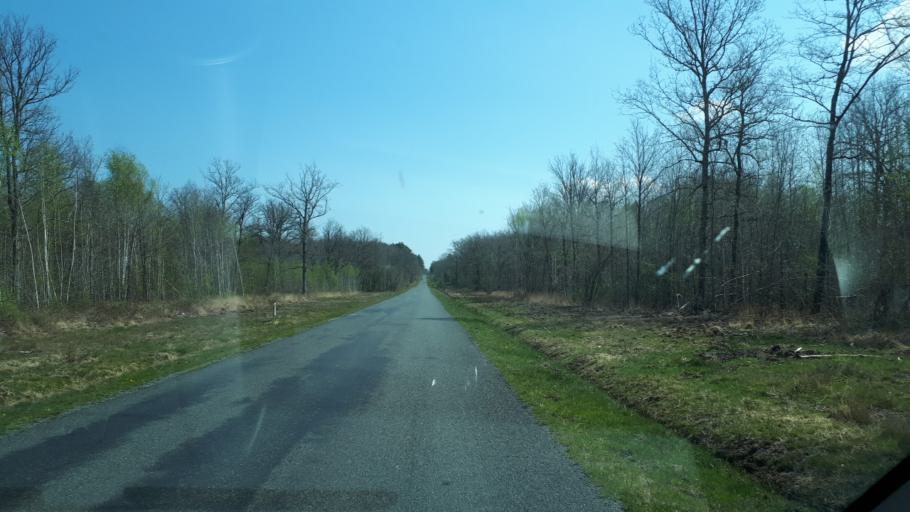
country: FR
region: Centre
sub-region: Departement du Cher
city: Neuvy-sur-Barangeon
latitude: 47.3191
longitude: 2.1660
